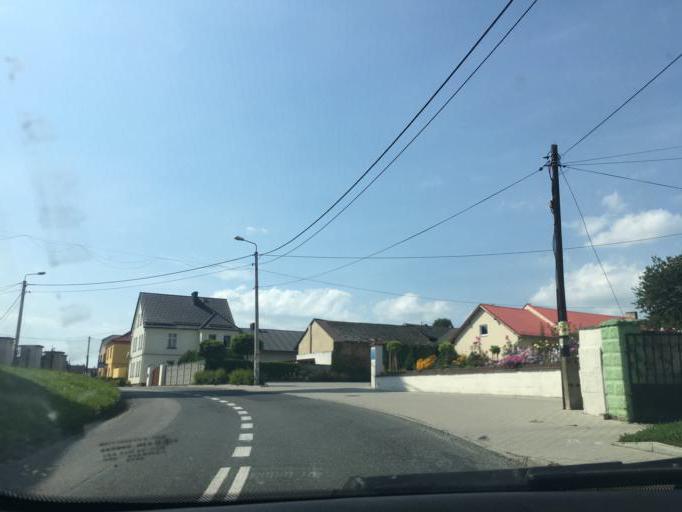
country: PL
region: Silesian Voivodeship
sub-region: Powiat raciborski
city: Pietrowice Wielkie
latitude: 50.0852
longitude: 18.0894
